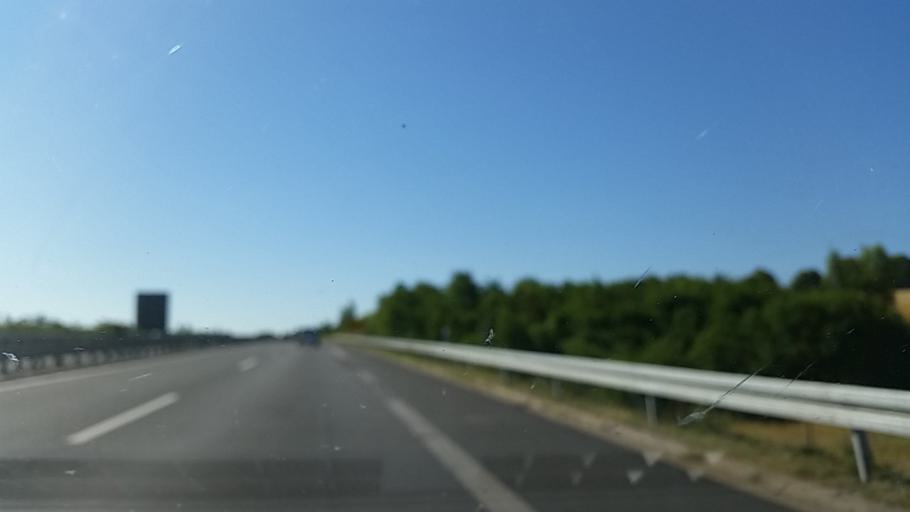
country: DE
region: Saxony-Anhalt
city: Blankenburg
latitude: 51.8202
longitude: 10.9290
